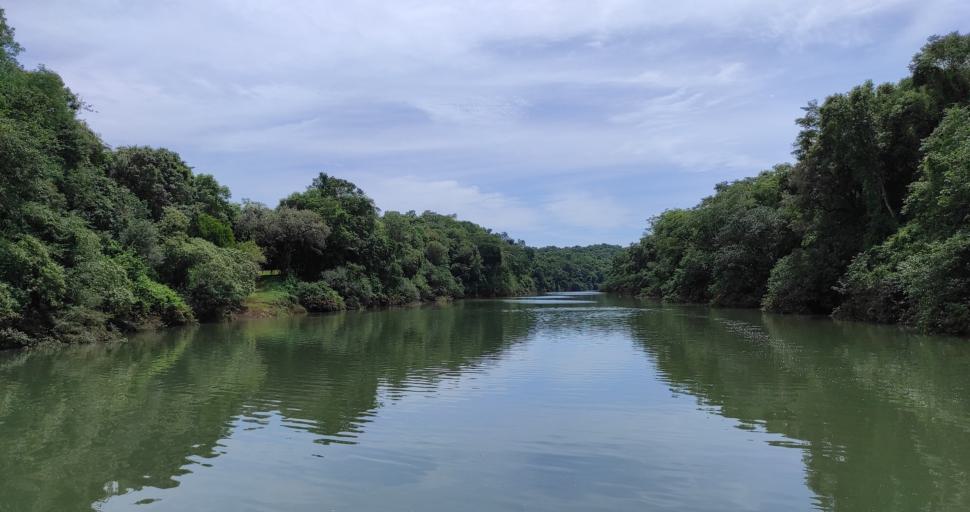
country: AR
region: Misiones
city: El Soberbio
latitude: -27.2778
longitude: -54.2209
